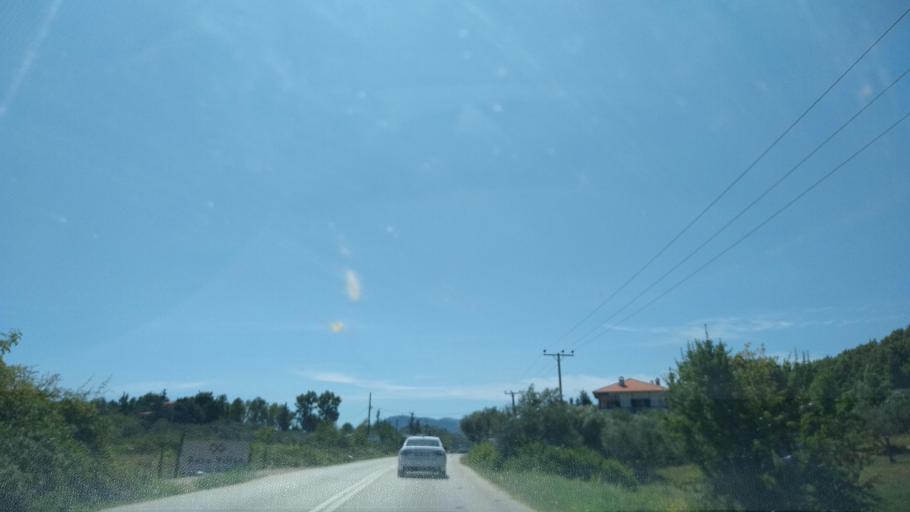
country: GR
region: Central Macedonia
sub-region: Nomos Chalkidikis
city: Agios Nikolaos
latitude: 40.2266
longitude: 23.7424
